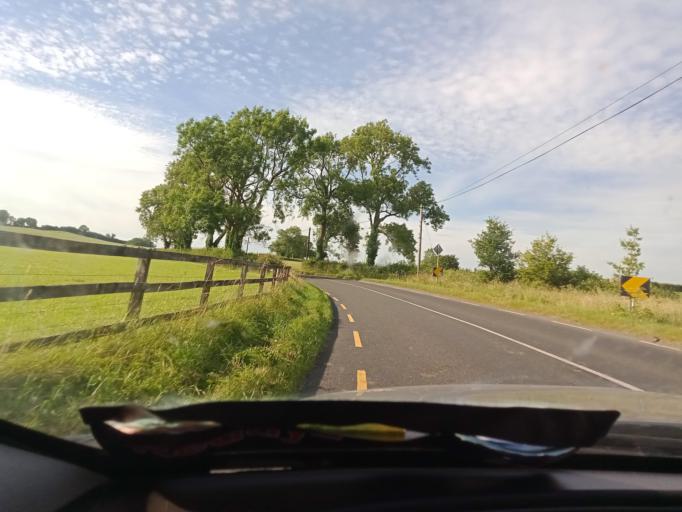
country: IE
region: Leinster
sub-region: An Iarmhi
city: Castlepollard
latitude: 53.6189
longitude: -7.2767
